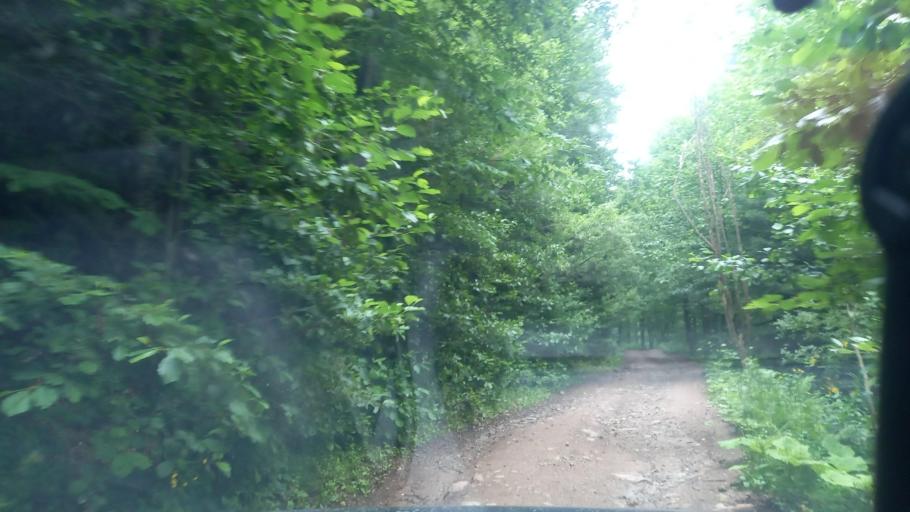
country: RU
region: Karachayevo-Cherkesiya
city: Kurdzhinovo
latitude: 43.8130
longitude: 40.8745
